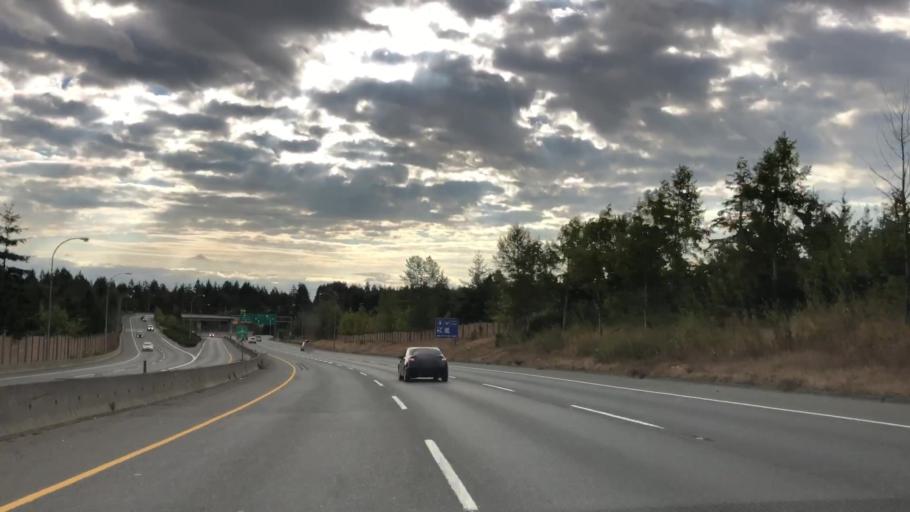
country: CA
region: British Columbia
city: Nanaimo
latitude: 49.1246
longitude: -123.9240
